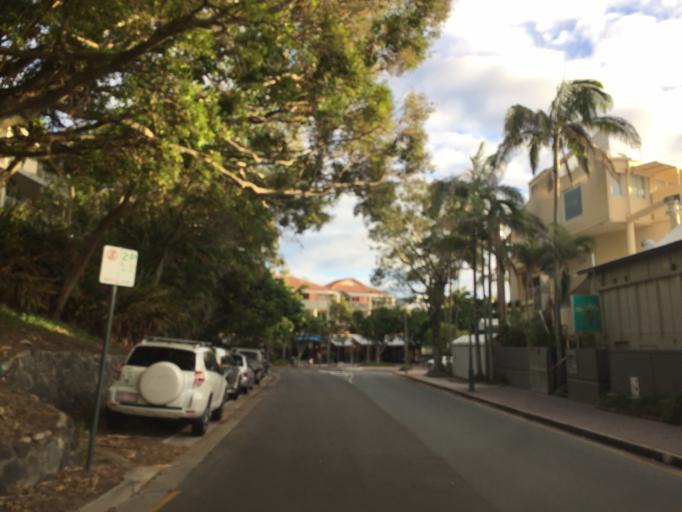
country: AU
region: Queensland
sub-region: Sunshine Coast
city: Noosa Heads
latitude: -26.3868
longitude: 153.0932
